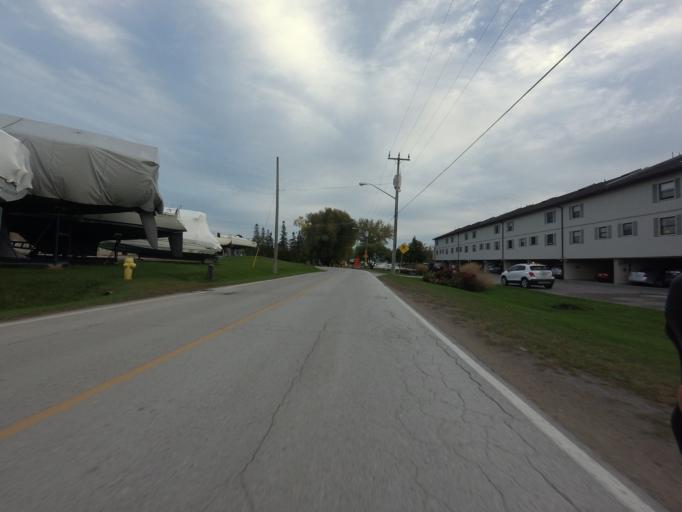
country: CA
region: Ontario
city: Oshawa
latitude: 43.8916
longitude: -78.6655
